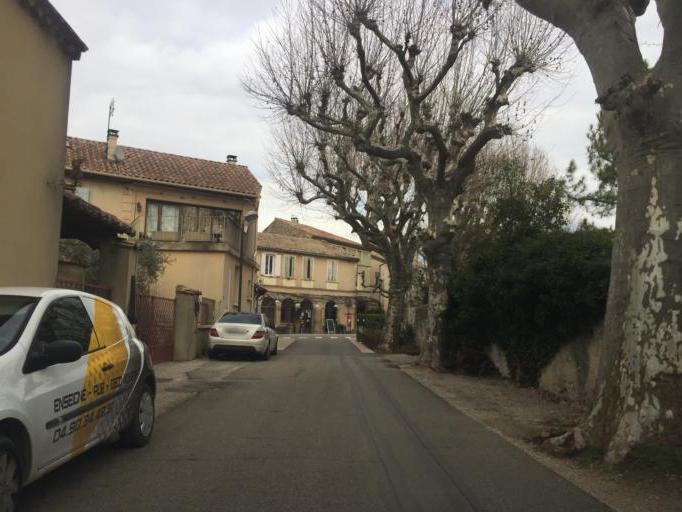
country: FR
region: Provence-Alpes-Cote d'Azur
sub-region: Departement du Vaucluse
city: Violes
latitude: 44.1614
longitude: 4.9537
